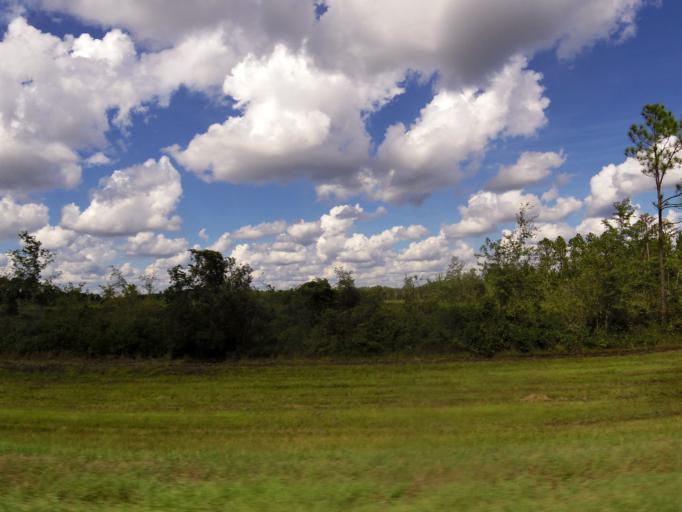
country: US
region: Florida
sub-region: Hamilton County
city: Jasper
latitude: 30.6743
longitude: -82.7723
